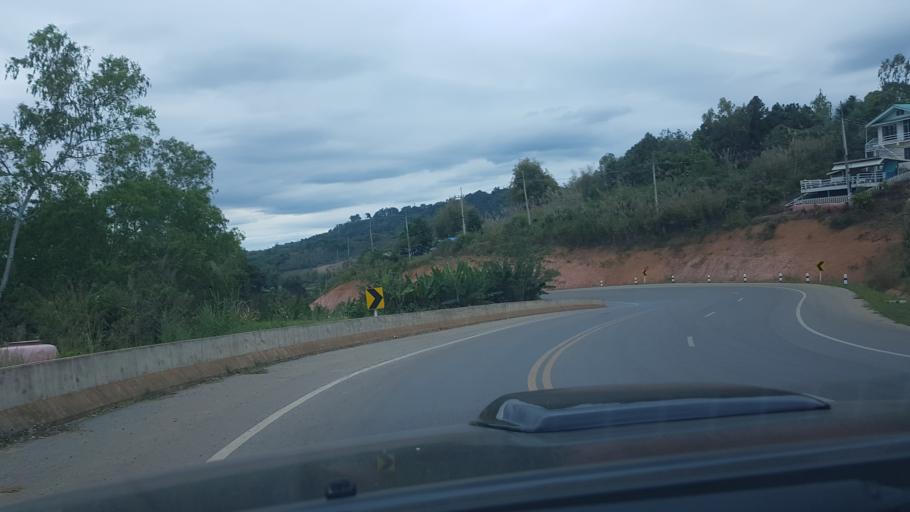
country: TH
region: Phetchabun
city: Khao Kho
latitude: 16.5701
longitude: 101.0054
